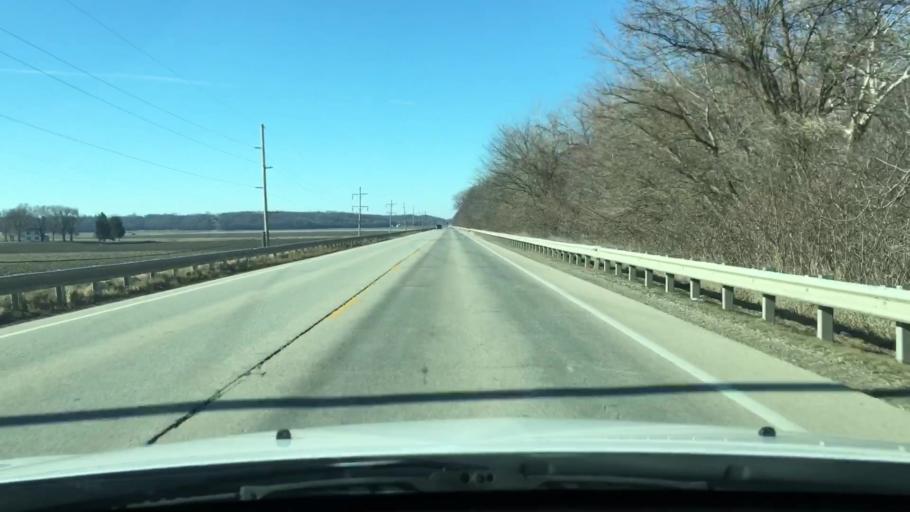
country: US
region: Illinois
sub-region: Mason County
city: Havana
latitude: 40.2988
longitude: -90.0980
